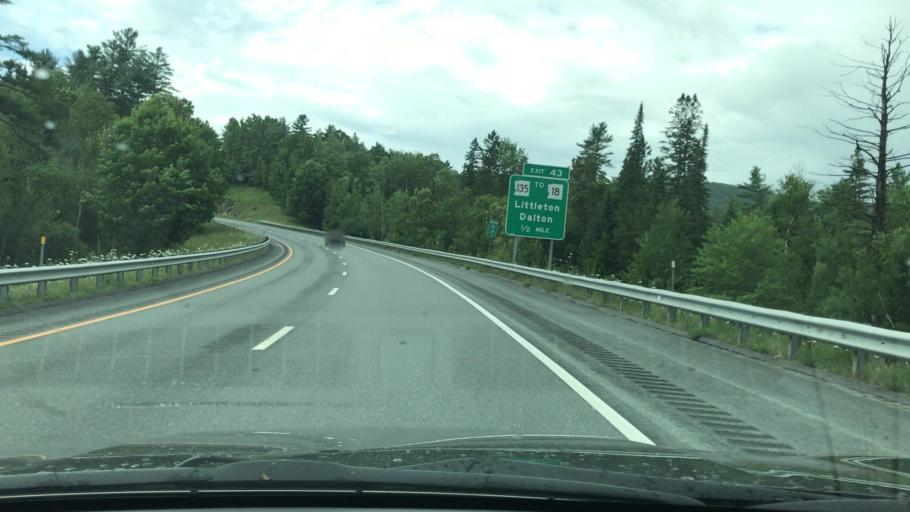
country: US
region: New Hampshire
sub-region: Grafton County
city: Littleton
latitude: 44.3220
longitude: -71.7961
